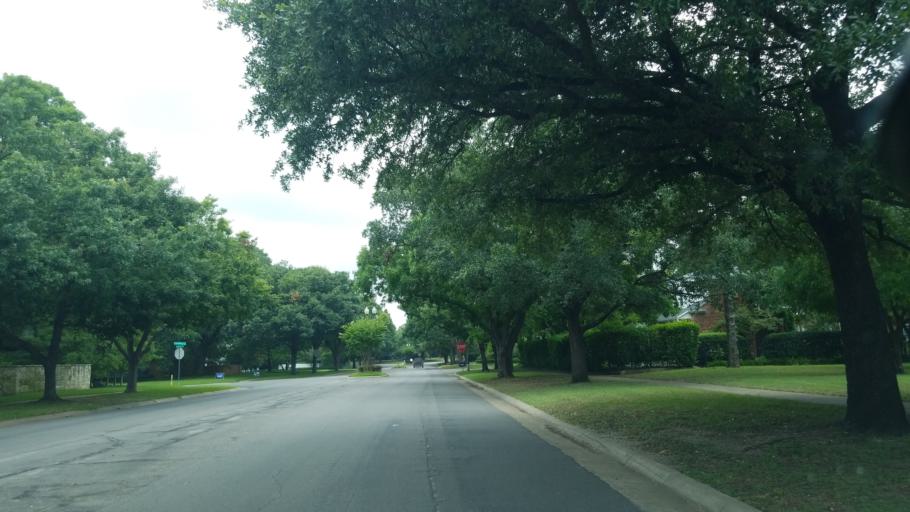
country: US
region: Texas
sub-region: Dallas County
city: University Park
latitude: 32.8394
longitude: -96.8178
